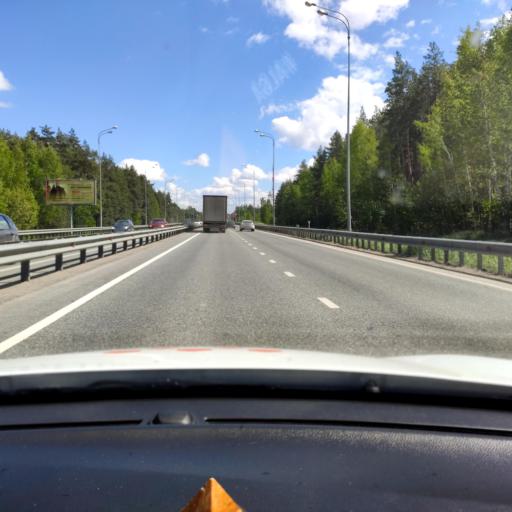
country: RU
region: Tatarstan
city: Staroye Arakchino
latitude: 55.8286
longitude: 49.0039
